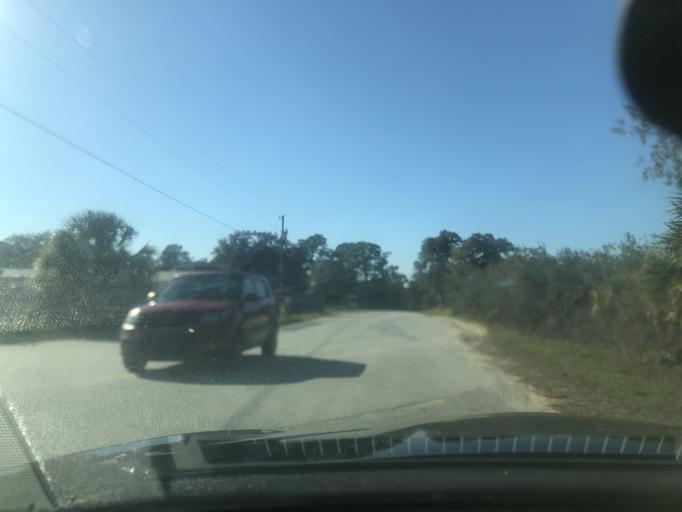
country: US
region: Florida
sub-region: Citrus County
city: Lecanto
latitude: 28.8259
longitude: -82.5241
